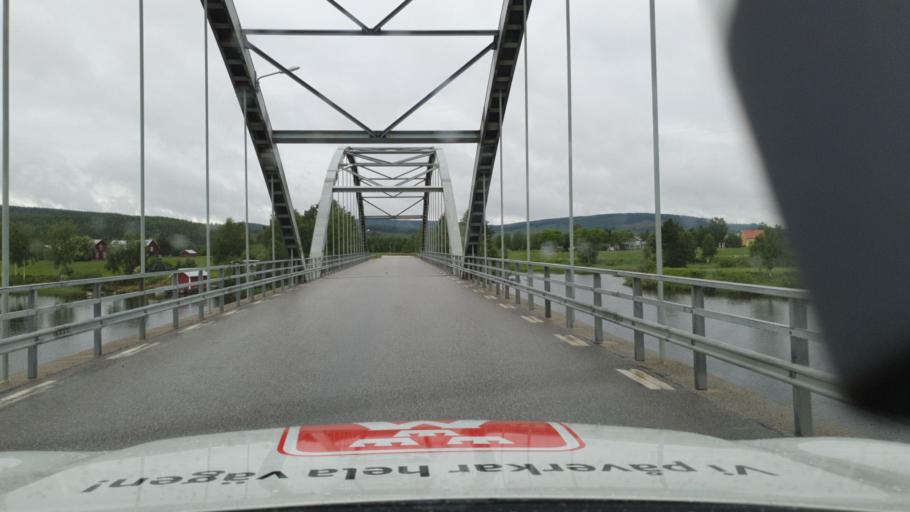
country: SE
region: Vaesterbotten
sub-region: Asele Kommun
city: Asele
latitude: 64.0085
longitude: 17.2636
